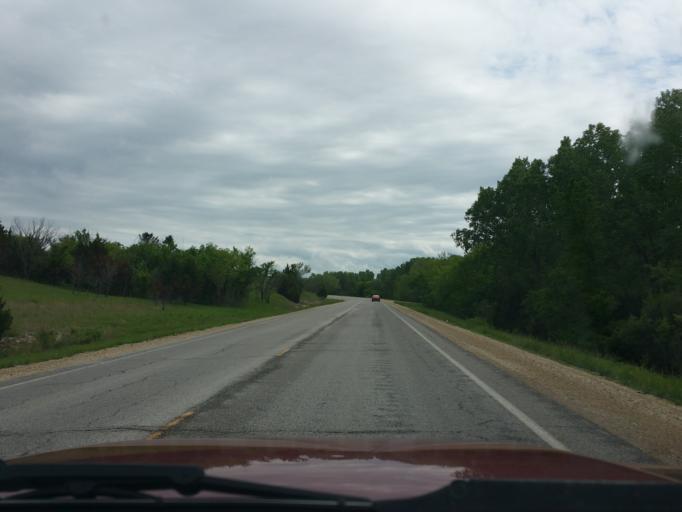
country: US
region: Kansas
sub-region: Riley County
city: Manhattan
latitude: 39.2390
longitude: -96.6228
